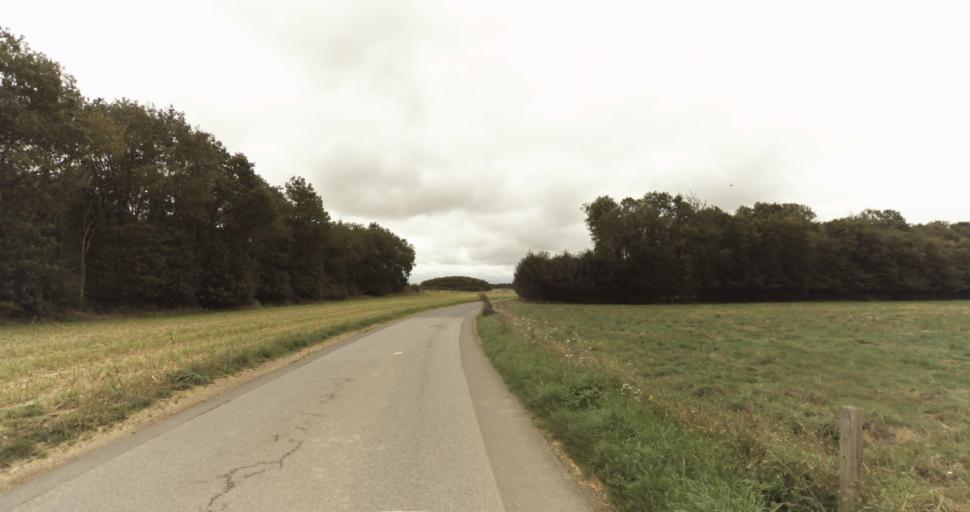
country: FR
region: Haute-Normandie
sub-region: Departement de l'Eure
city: Evreux
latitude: 48.9295
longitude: 1.2027
